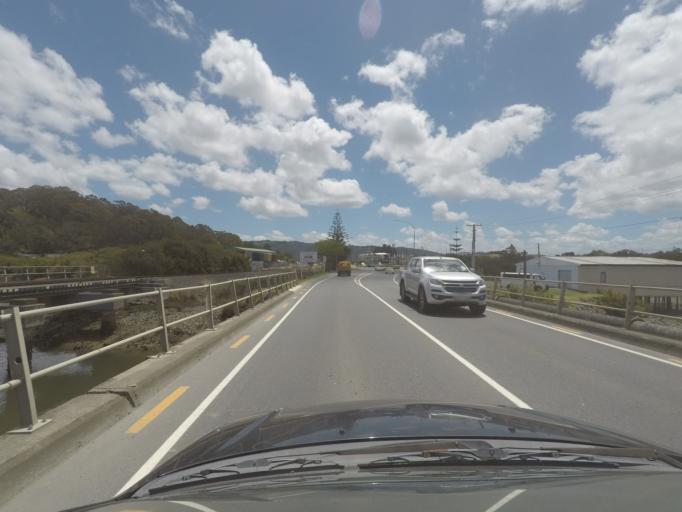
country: NZ
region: Northland
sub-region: Whangarei
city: Whangarei
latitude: -35.7381
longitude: 174.3337
